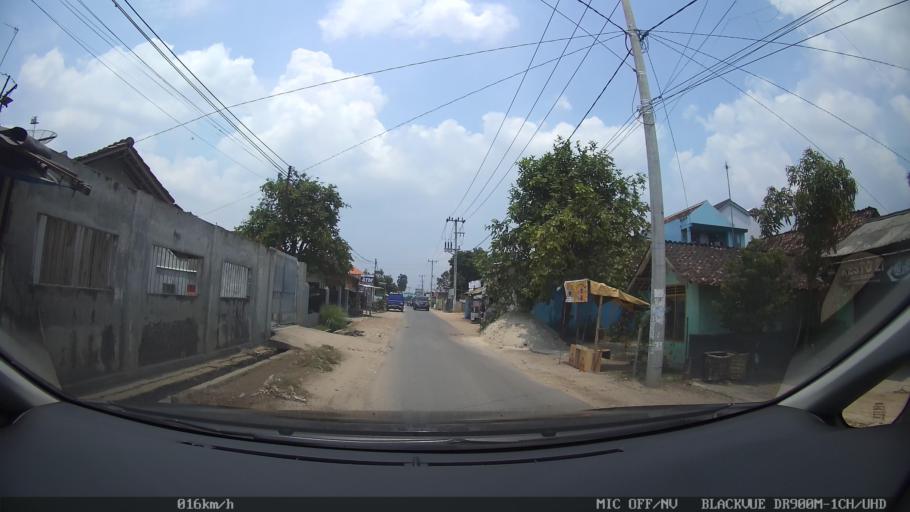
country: ID
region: Lampung
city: Pringsewu
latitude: -5.3498
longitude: 104.9808
